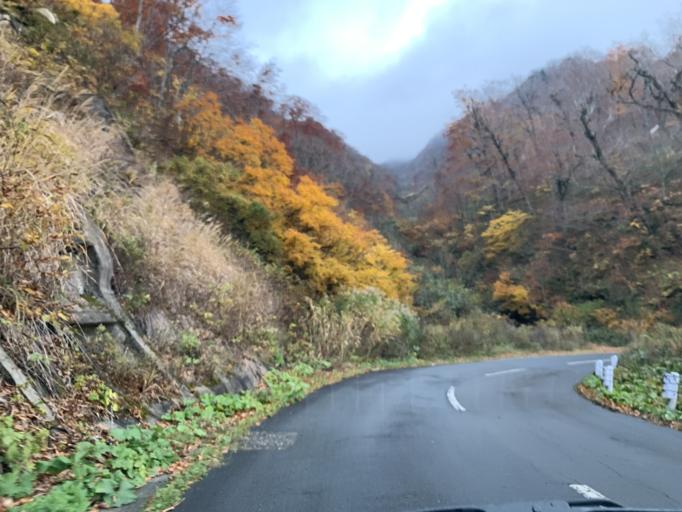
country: JP
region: Iwate
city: Mizusawa
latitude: 39.1273
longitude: 140.8248
